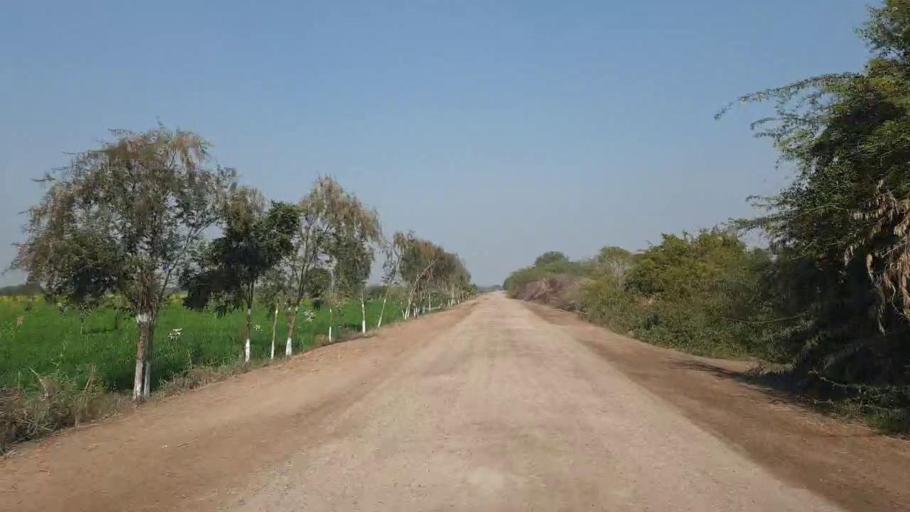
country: PK
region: Sindh
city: Mirwah Gorchani
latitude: 25.3736
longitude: 68.9317
